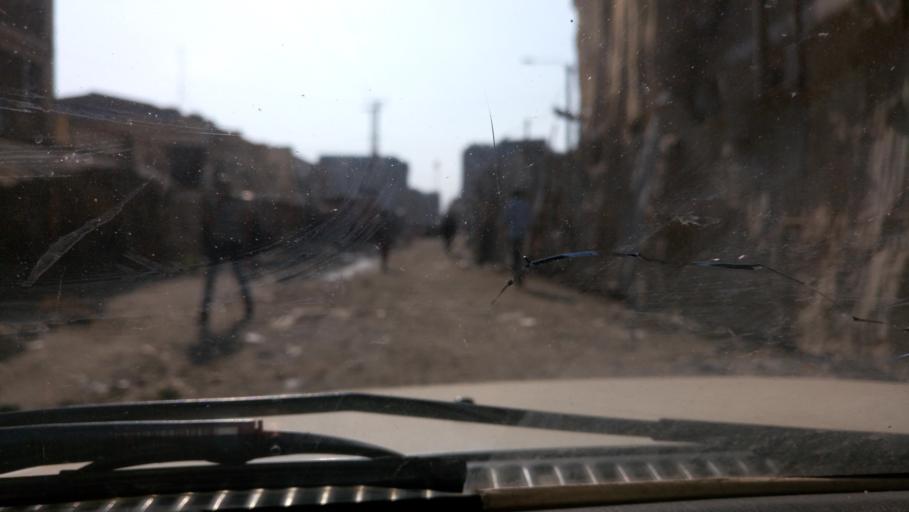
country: KE
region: Nairobi Area
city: Pumwani
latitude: -1.2721
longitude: 36.8459
